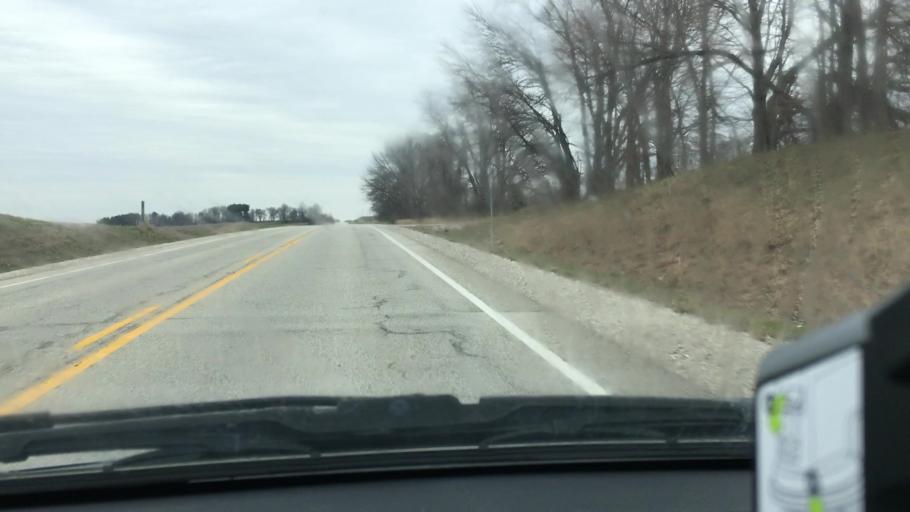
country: US
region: Indiana
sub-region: Greene County
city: Bloomfield
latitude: 38.9546
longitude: -87.0167
